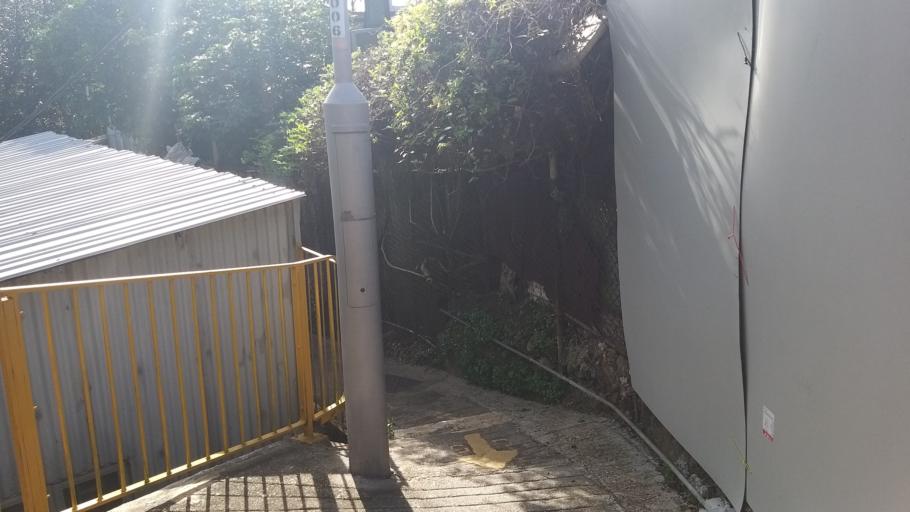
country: HK
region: Tuen Mun
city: Tuen Mun
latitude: 22.3947
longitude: 113.9805
